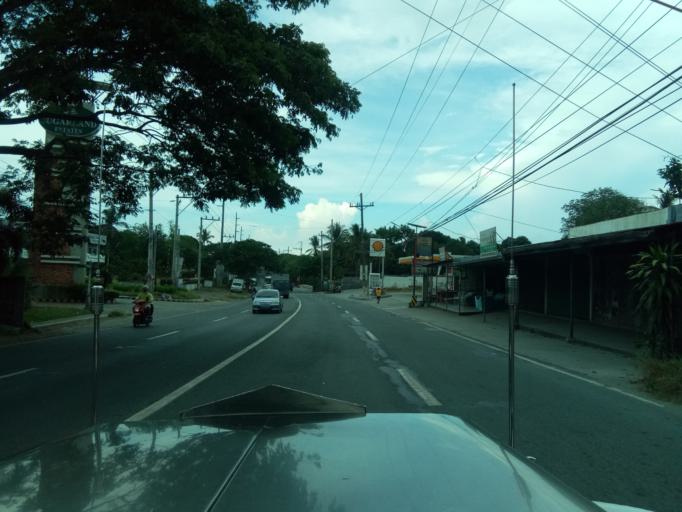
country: PH
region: Calabarzon
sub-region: Province of Cavite
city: Aliang
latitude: 14.2805
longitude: 120.8863
